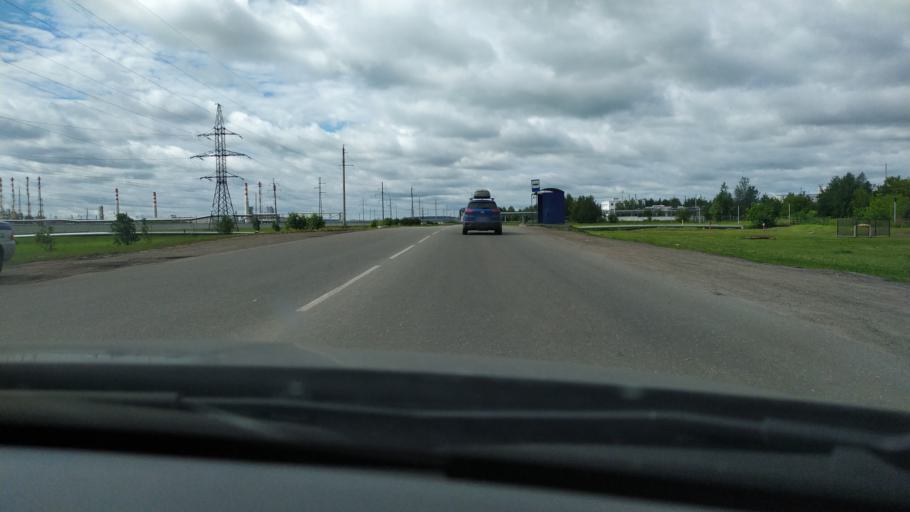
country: RU
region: Perm
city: Kondratovo
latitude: 57.9318
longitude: 56.1254
